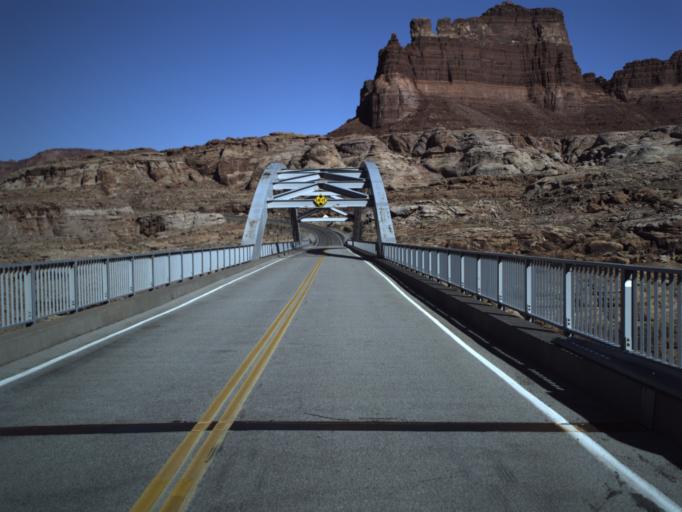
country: US
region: Utah
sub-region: San Juan County
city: Blanding
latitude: 37.8902
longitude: -110.3698
